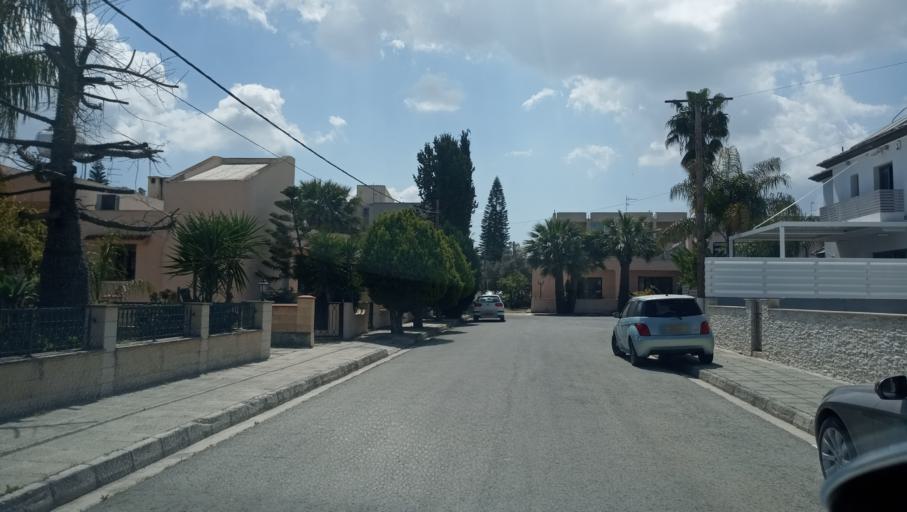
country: CY
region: Lefkosia
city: Dali
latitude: 35.0183
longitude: 33.4091
